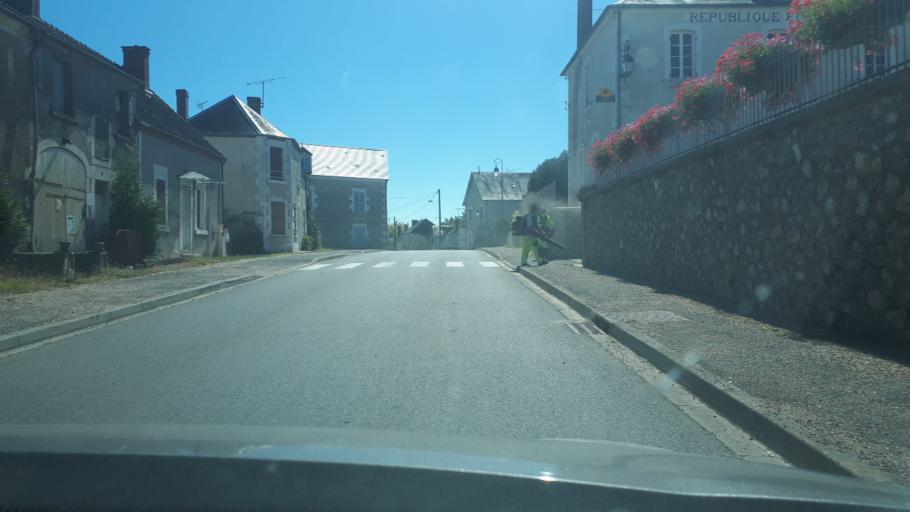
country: FR
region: Centre
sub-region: Departement du Cher
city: Sancerre
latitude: 47.2567
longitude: 2.7581
